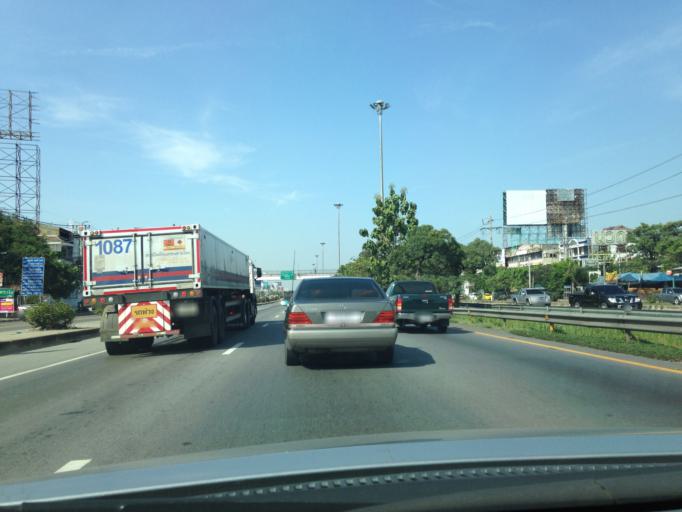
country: TH
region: Nonthaburi
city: Bang Yai
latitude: 13.8362
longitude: 100.4135
